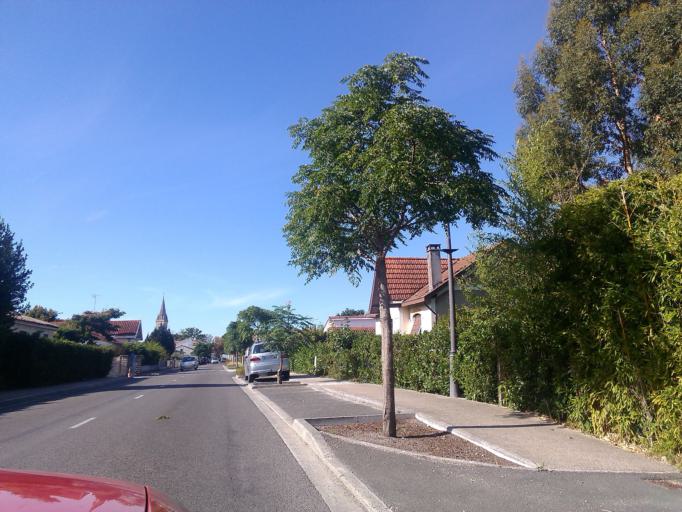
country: FR
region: Aquitaine
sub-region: Departement de la Gironde
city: Hourtin
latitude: 45.1830
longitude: -1.0565
